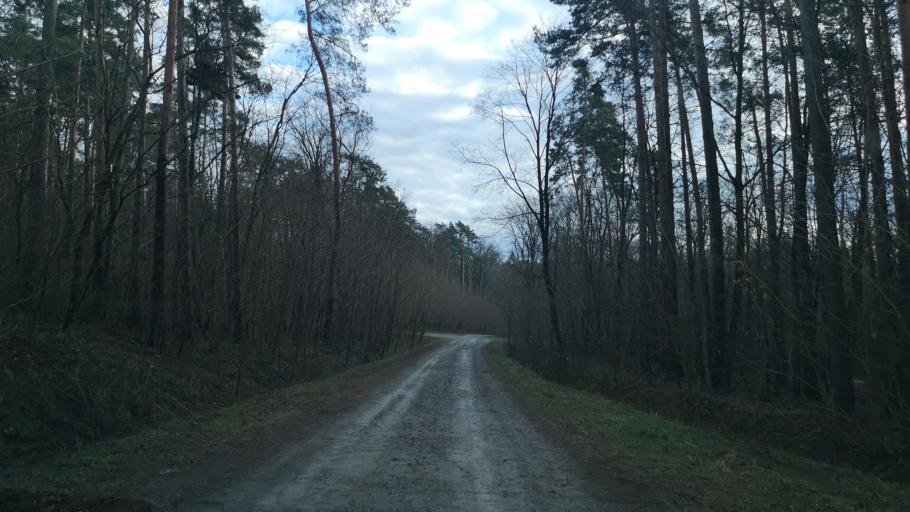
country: PL
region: Subcarpathian Voivodeship
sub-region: Powiat lezajski
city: Piskorowice
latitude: 50.2504
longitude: 22.5709
